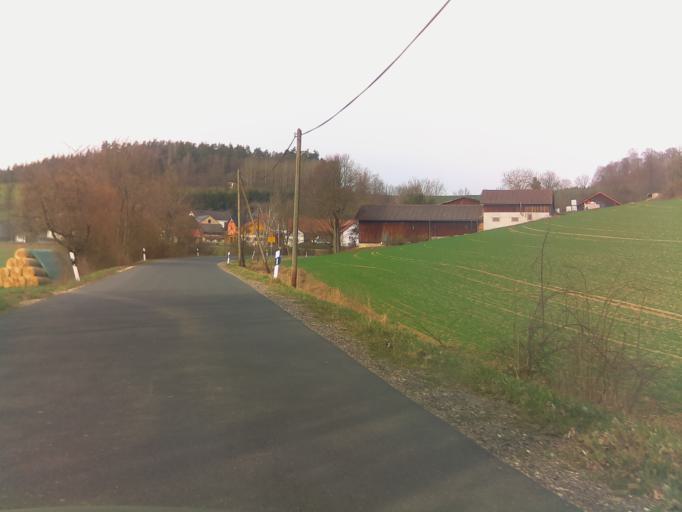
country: DE
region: Bavaria
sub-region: Upper Palatinate
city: Freudenberg
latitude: 49.4783
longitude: 12.0506
